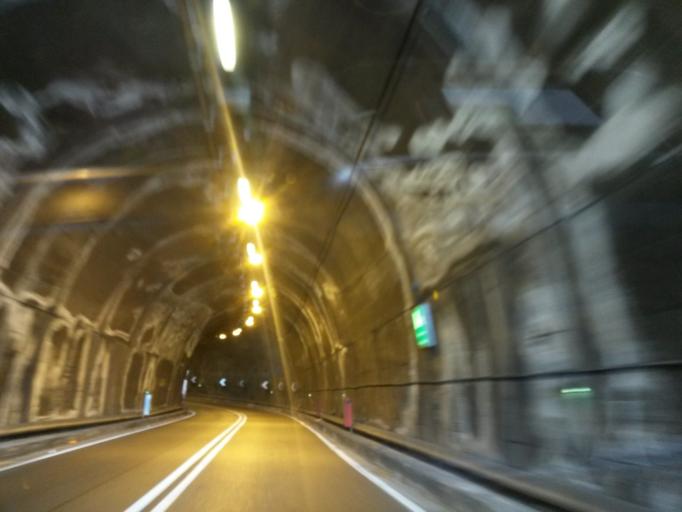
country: IT
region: Lombardy
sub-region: Provincia di Brescia
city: Gardola
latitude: 45.7124
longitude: 10.6999
